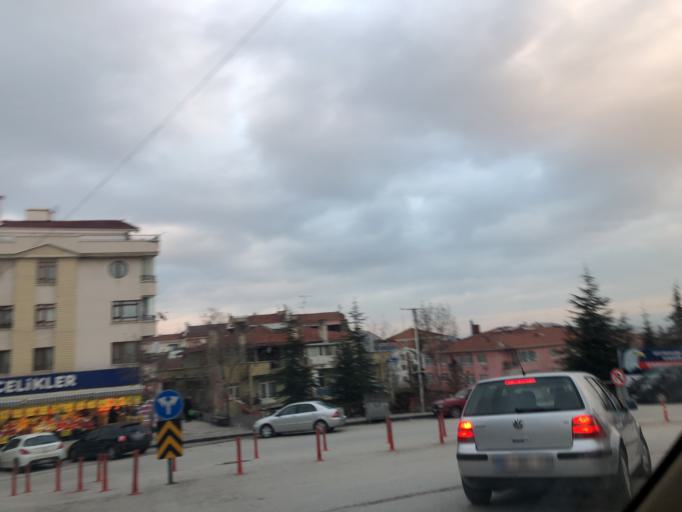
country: TR
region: Ankara
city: Ankara
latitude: 39.9694
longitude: 32.8082
